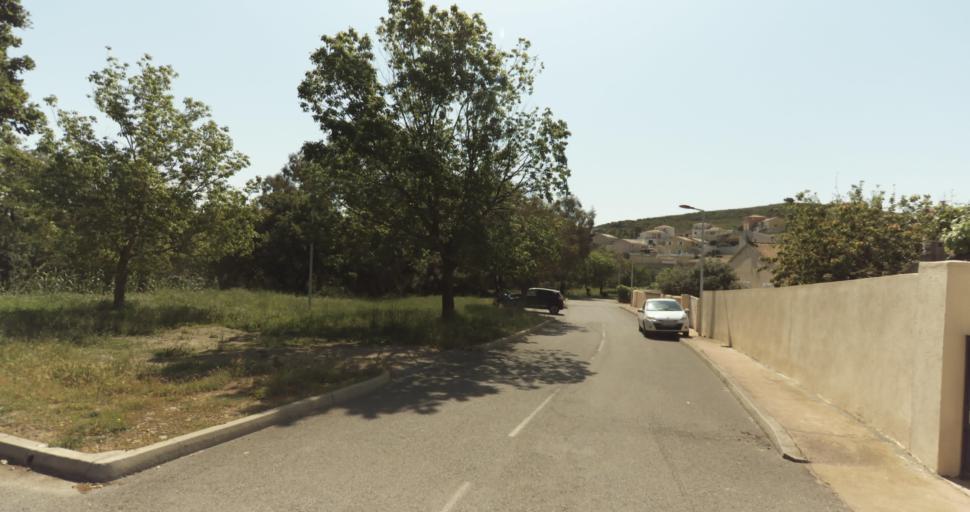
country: FR
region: Corsica
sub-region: Departement de la Haute-Corse
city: Biguglia
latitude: 42.6210
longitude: 9.4265
